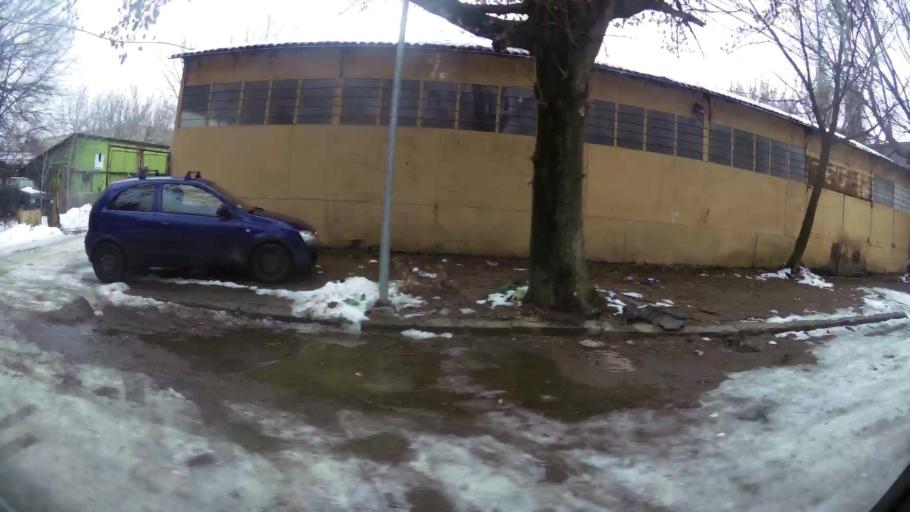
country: RO
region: Ilfov
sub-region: Comuna Popesti-Leordeni
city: Popesti-Leordeni
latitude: 44.4038
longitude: 26.1472
